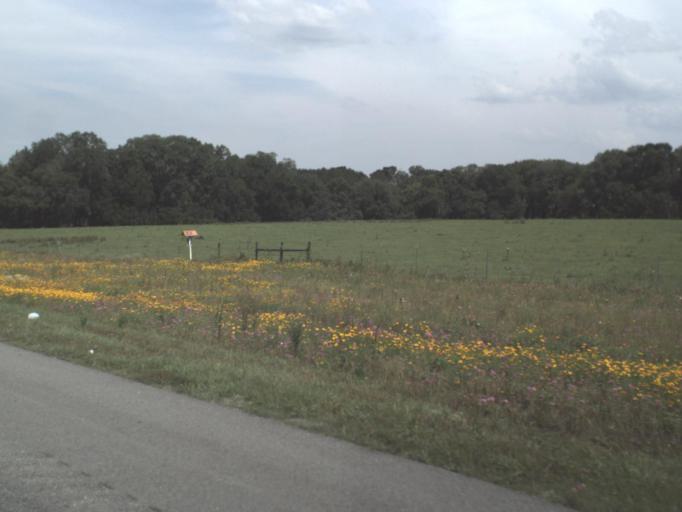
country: US
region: Florida
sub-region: Suwannee County
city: Live Oak
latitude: 30.3507
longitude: -83.0469
